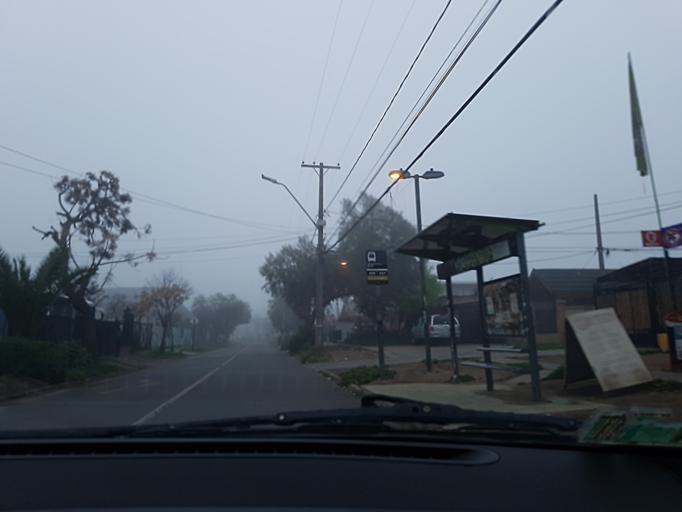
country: CL
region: Santiago Metropolitan
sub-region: Provincia de Santiago
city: Lo Prado
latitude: -33.4746
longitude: -70.7012
